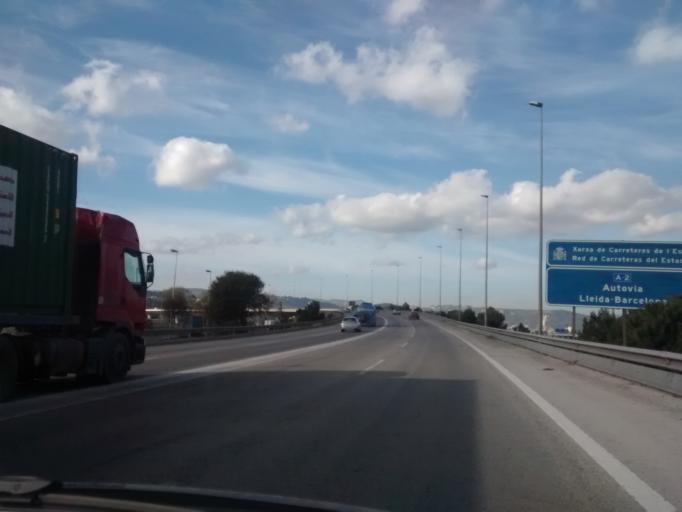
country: ES
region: Catalonia
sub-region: Provincia de Barcelona
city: Sant Feliu de Llobregat
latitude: 41.3765
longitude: 2.0362
